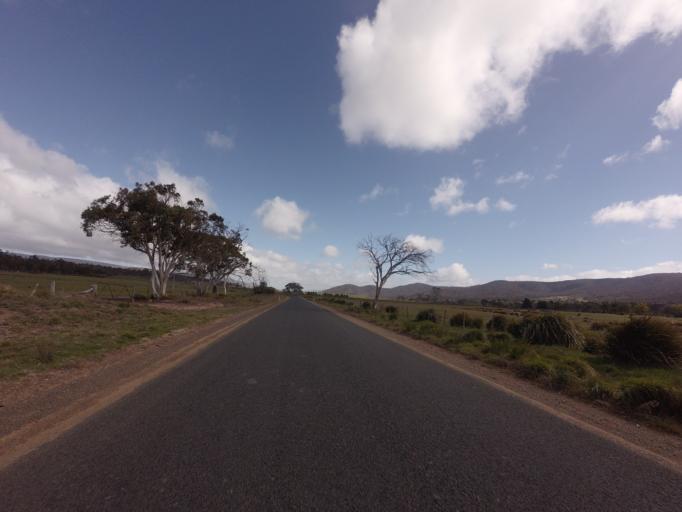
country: AU
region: Tasmania
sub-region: Northern Midlands
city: Evandale
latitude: -41.8239
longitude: 147.8280
